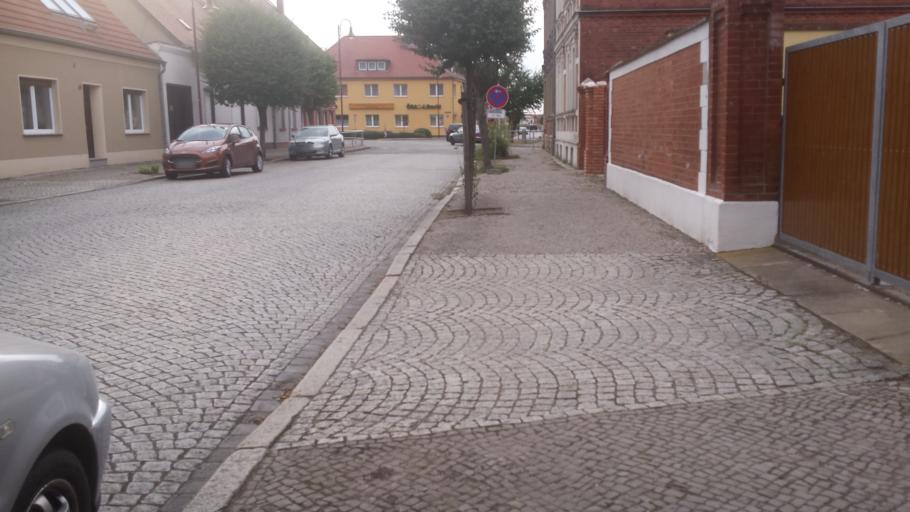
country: DE
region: Saxony-Anhalt
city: Tangermunde
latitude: 52.5458
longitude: 11.9774
